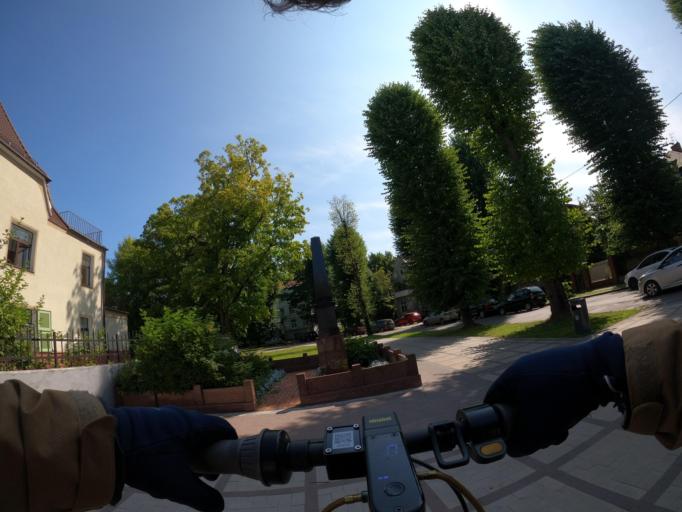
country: RU
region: Kaliningrad
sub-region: Gorod Kaliningrad
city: Kaliningrad
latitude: 54.7362
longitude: 20.5242
